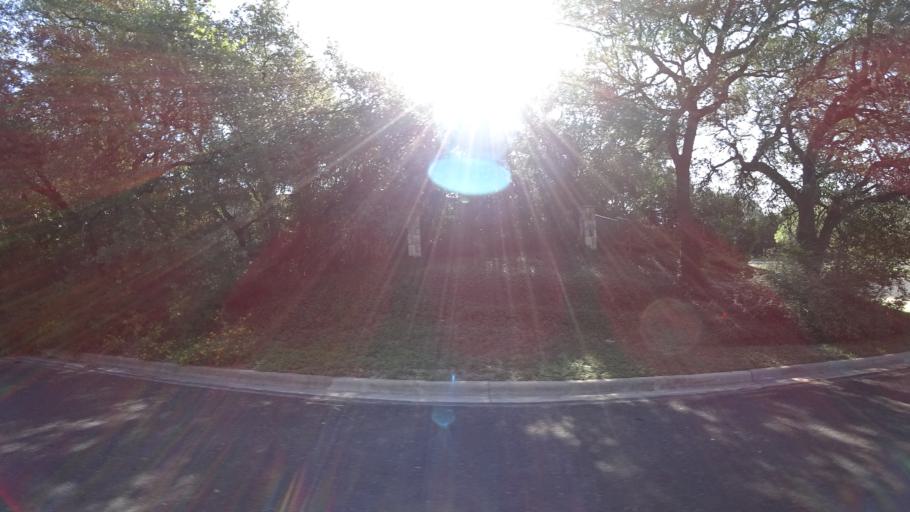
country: US
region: Texas
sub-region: Travis County
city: Rollingwood
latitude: 30.2661
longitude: -97.7885
